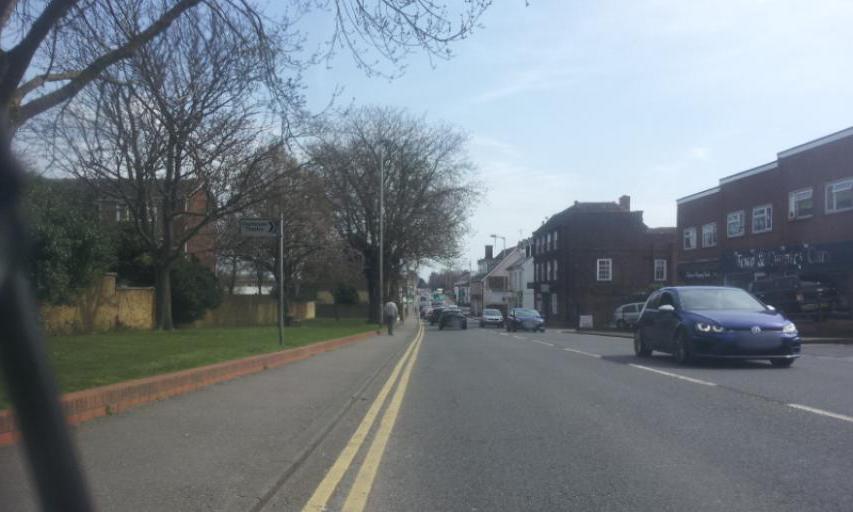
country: GB
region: England
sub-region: Kent
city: Rainham
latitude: 51.3625
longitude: 0.6121
